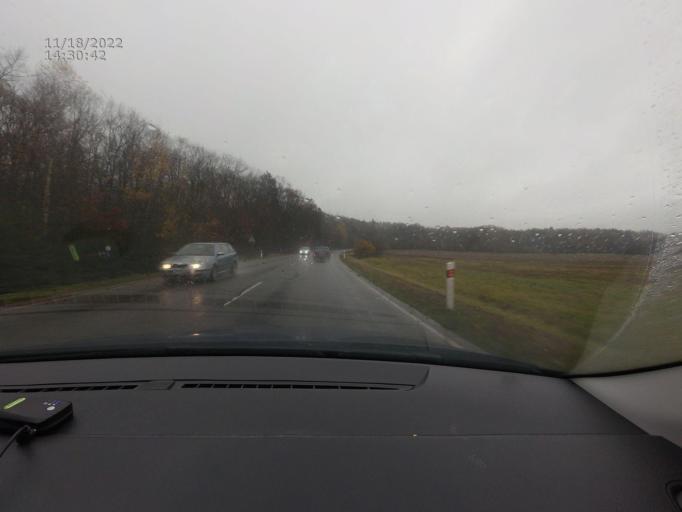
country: CZ
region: Jihocesky
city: Kovarov
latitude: 49.4500
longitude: 14.2518
